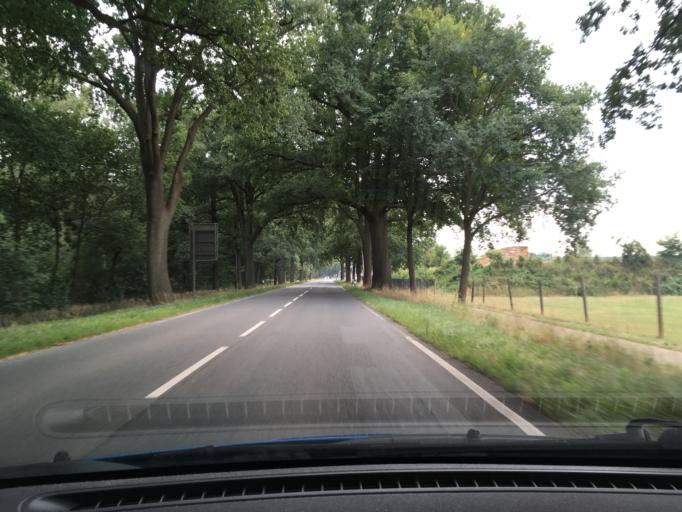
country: DE
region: Lower Saxony
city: Adelheidsdorf
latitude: 52.5622
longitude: 10.0588
